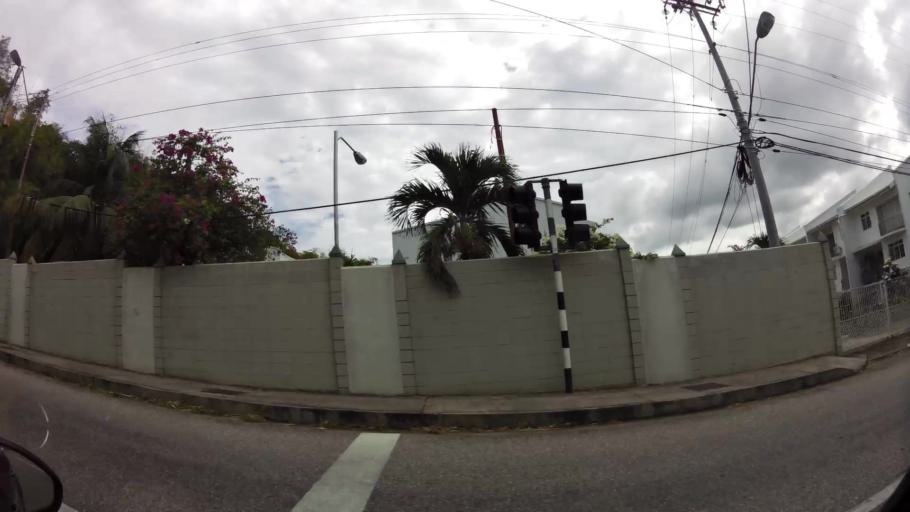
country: TT
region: City of Port of Spain
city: Port-of-Spain
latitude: 10.6798
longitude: -61.5302
